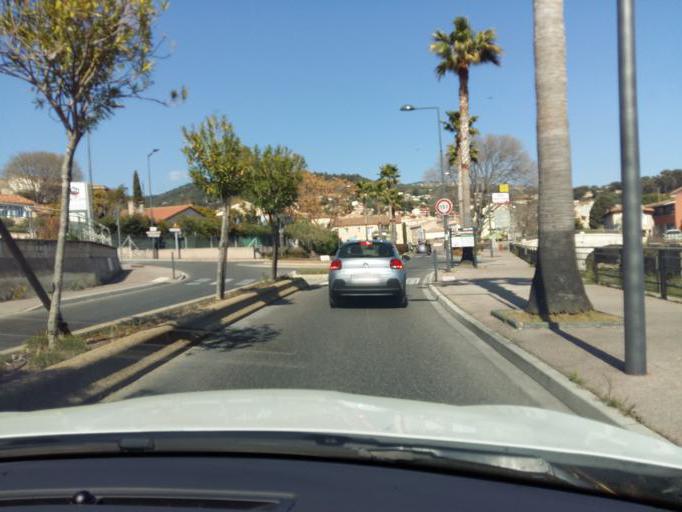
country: FR
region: Provence-Alpes-Cote d'Azur
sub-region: Departement du Var
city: Ollioules
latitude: 43.1348
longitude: 5.8463
